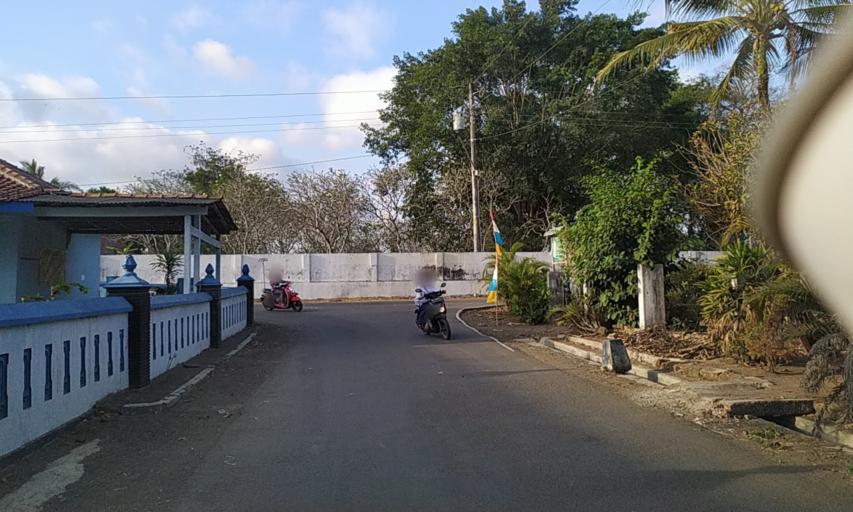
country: ID
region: Central Java
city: Adipala
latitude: -7.6542
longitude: 109.1377
